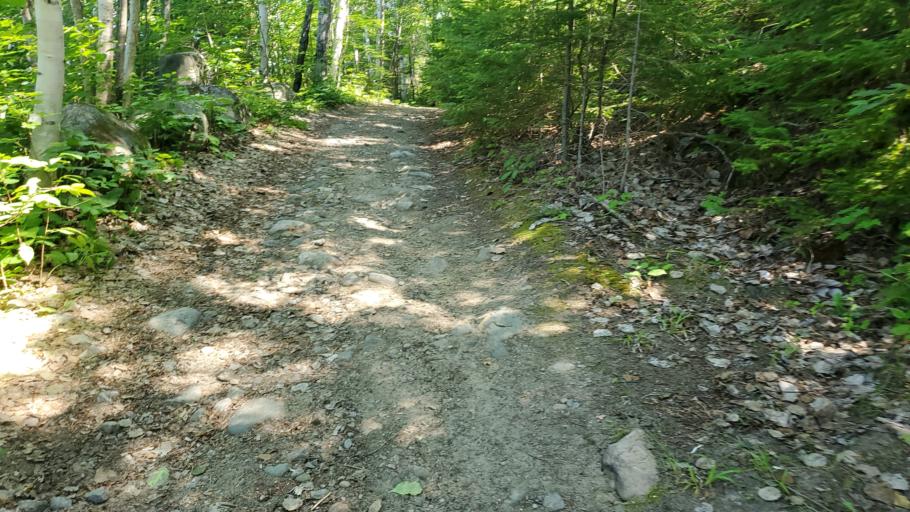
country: CA
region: Ontario
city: Mattawa
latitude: 46.2596
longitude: -78.2762
